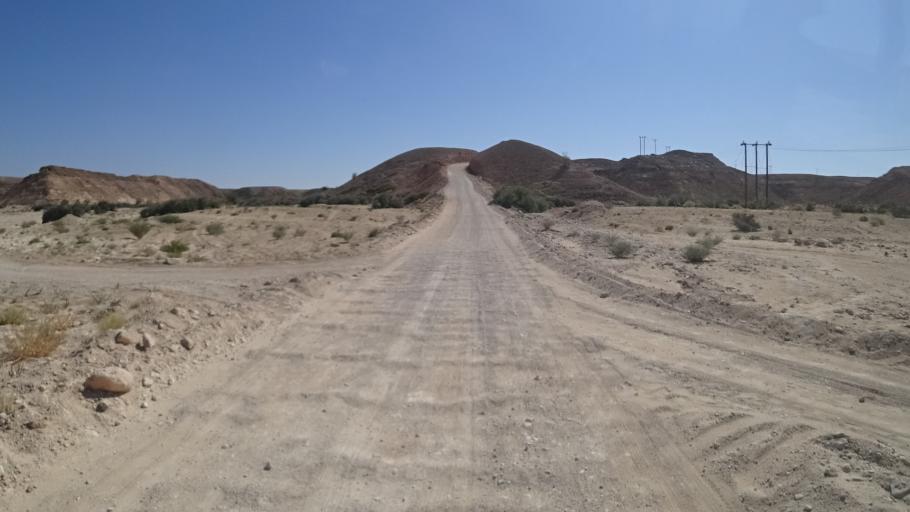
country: YE
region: Al Mahrah
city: Hawf
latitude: 17.3736
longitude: 53.1929
